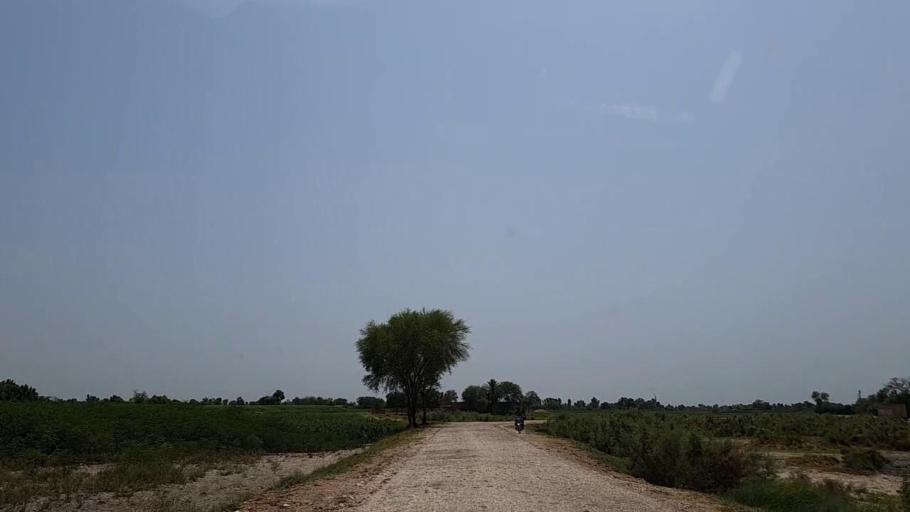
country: PK
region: Sindh
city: Adilpur
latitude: 27.9722
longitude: 69.3977
